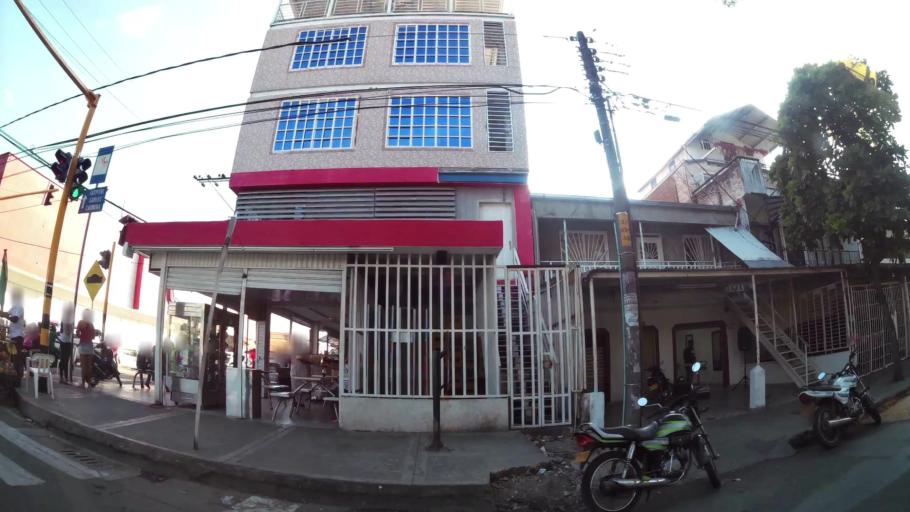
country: CO
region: Valle del Cauca
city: Cali
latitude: 3.4138
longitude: -76.5096
